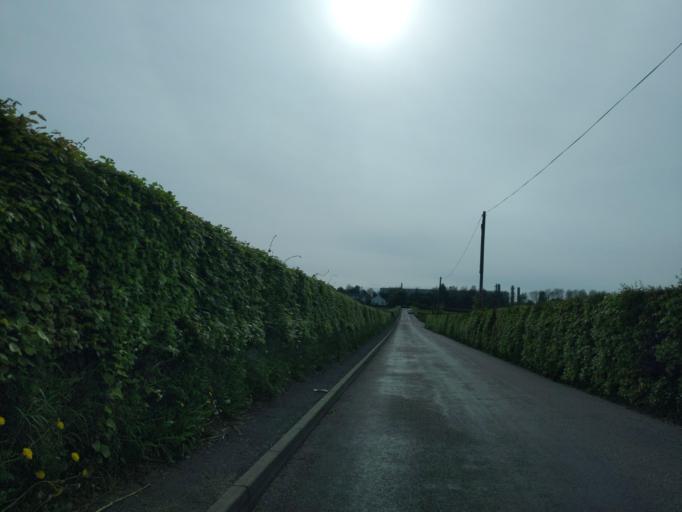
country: GB
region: England
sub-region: Devon
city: Yelverton
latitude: 50.4438
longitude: -4.1035
